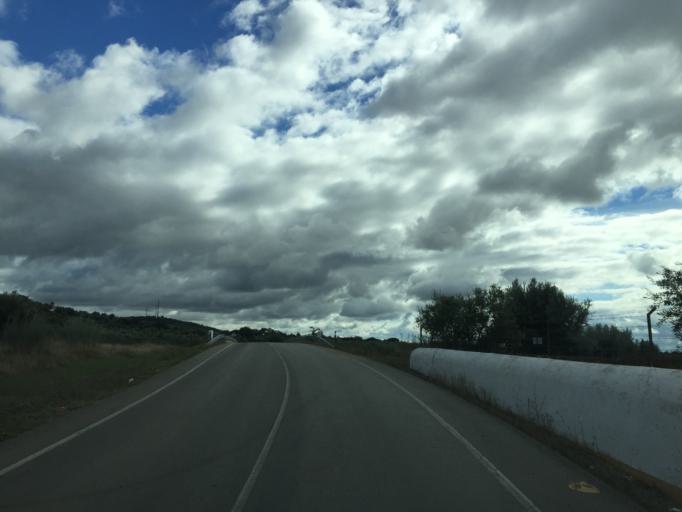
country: PT
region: Portalegre
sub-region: Alter do Chao
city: Alter do Chao
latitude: 39.2208
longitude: -7.6719
